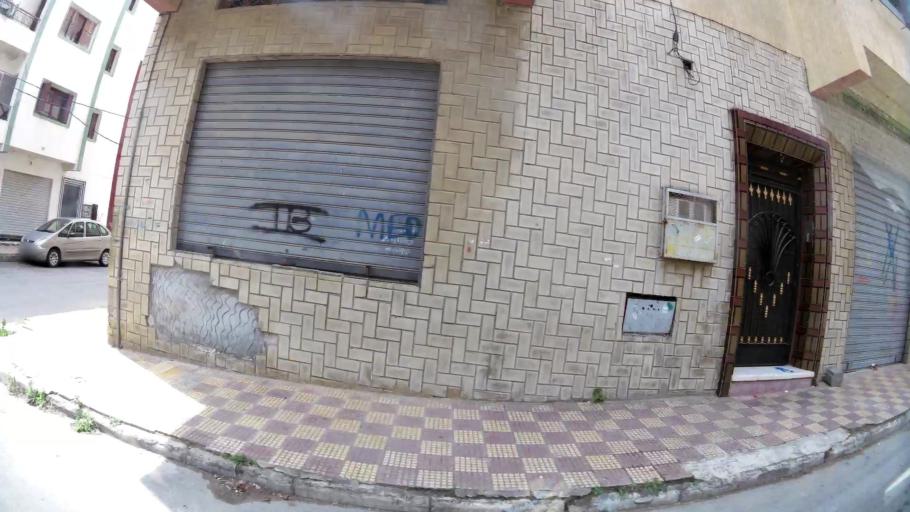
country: MA
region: Tanger-Tetouan
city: Tetouan
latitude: 35.5851
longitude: -5.3429
